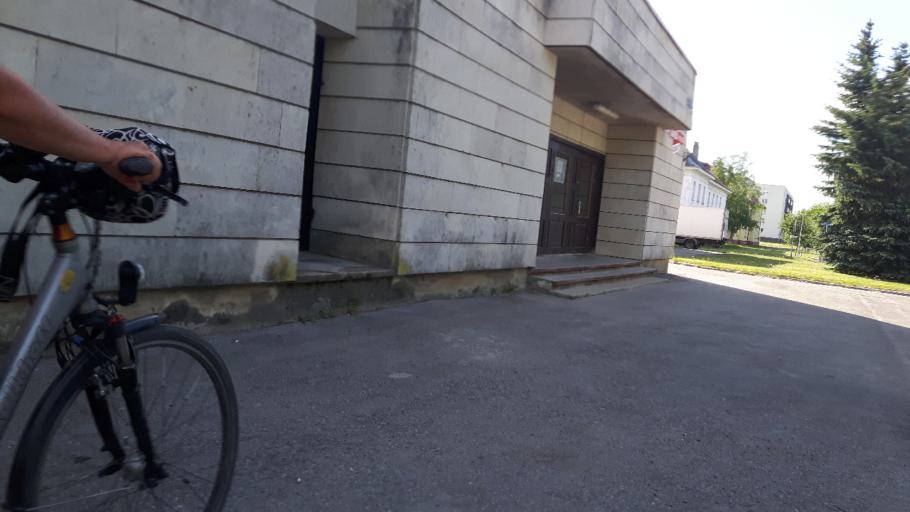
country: EE
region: Harju
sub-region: Joelaehtme vald
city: Loo
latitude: 59.4340
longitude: 24.9472
